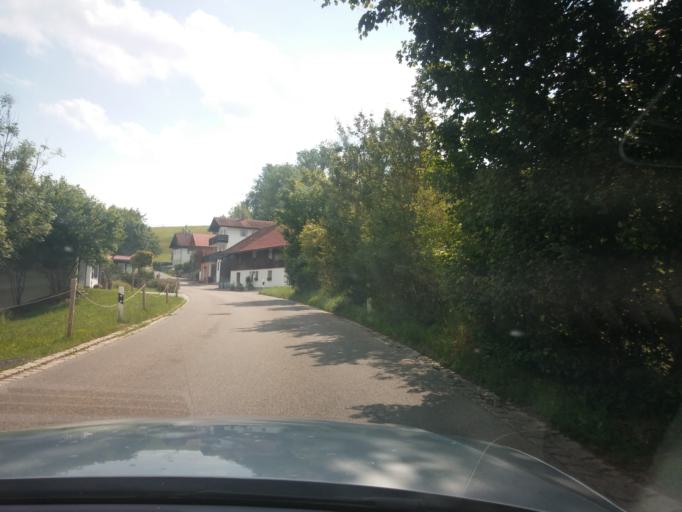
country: DE
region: Bavaria
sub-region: Swabia
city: Altusried
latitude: 47.7965
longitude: 10.2152
